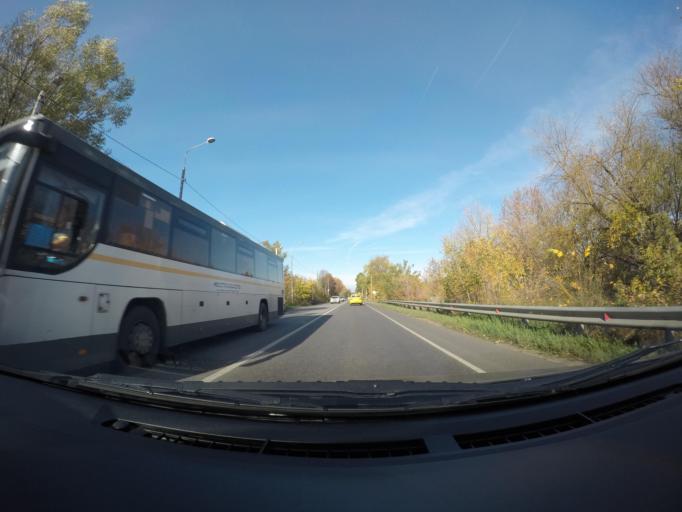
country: RU
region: Moskovskaya
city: Gzhel'
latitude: 55.6186
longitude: 38.3819
